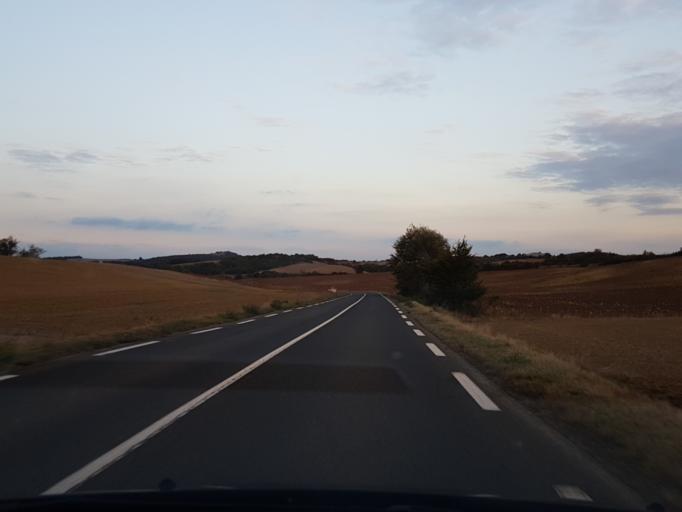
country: FR
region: Midi-Pyrenees
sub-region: Departement de l'Ariege
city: Mirepoix
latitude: 43.1520
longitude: 1.9681
